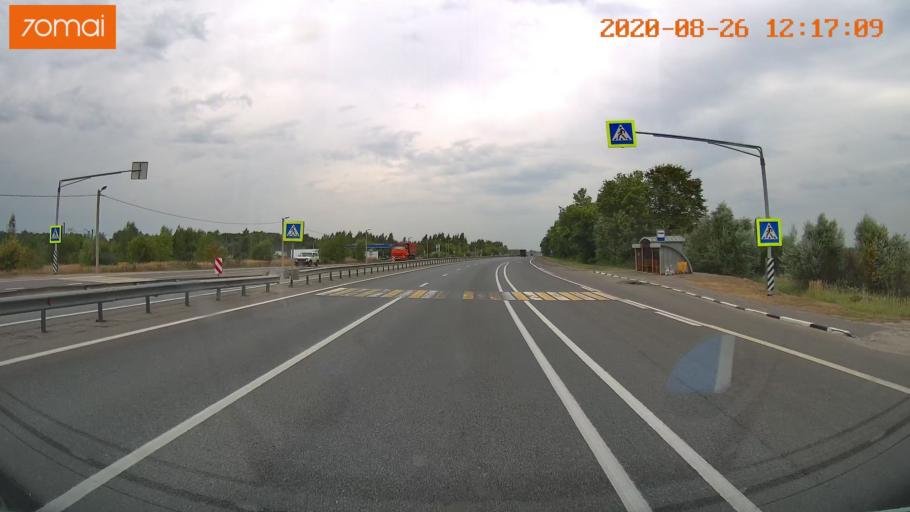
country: RU
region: Rjazan
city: Murmino
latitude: 54.4564
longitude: 40.0328
